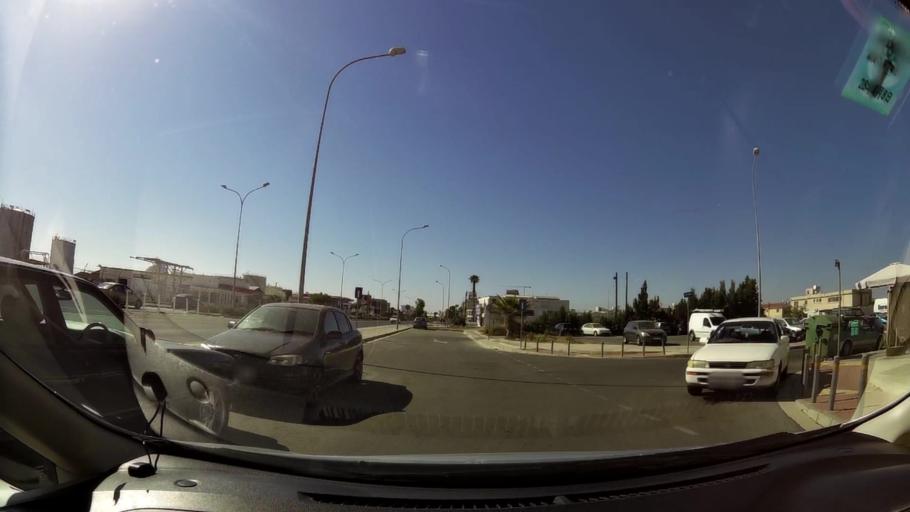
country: CY
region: Larnaka
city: Livadia
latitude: 34.9384
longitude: 33.6410
